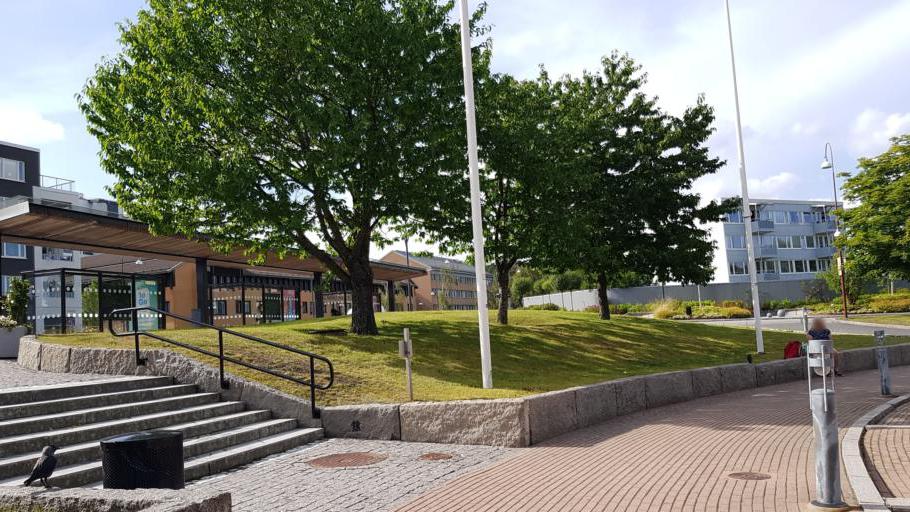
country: SE
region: Vaestra Goetaland
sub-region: Harryda Kommun
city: Molnlycke
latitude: 57.6592
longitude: 12.1184
